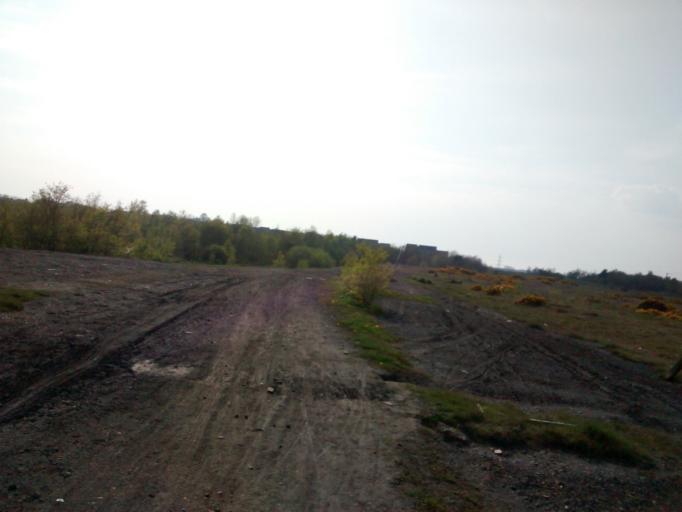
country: GB
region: England
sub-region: County Durham
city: South Hetton
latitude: 54.8016
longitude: -1.4040
